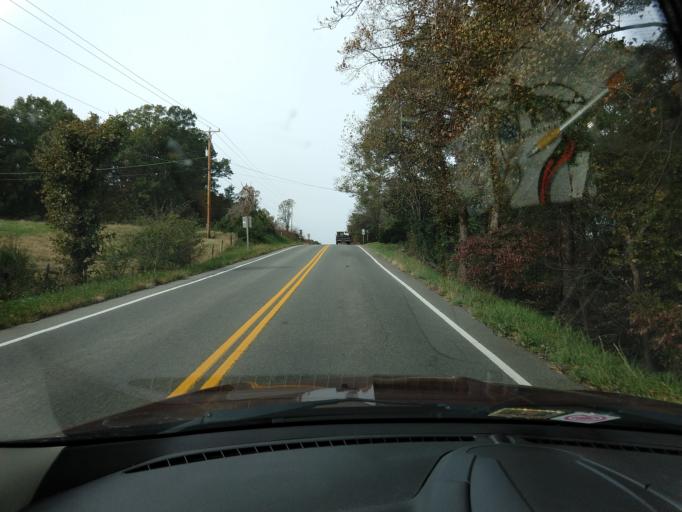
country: US
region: Virginia
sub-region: Franklin County
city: Union Hall
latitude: 36.9876
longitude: -79.6532
